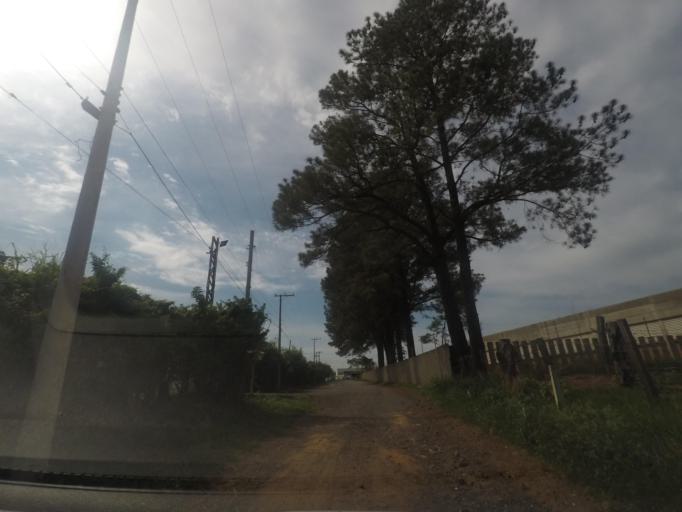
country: BR
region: Sao Paulo
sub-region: Sumare
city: Sumare
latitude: -22.8001
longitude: -47.2394
